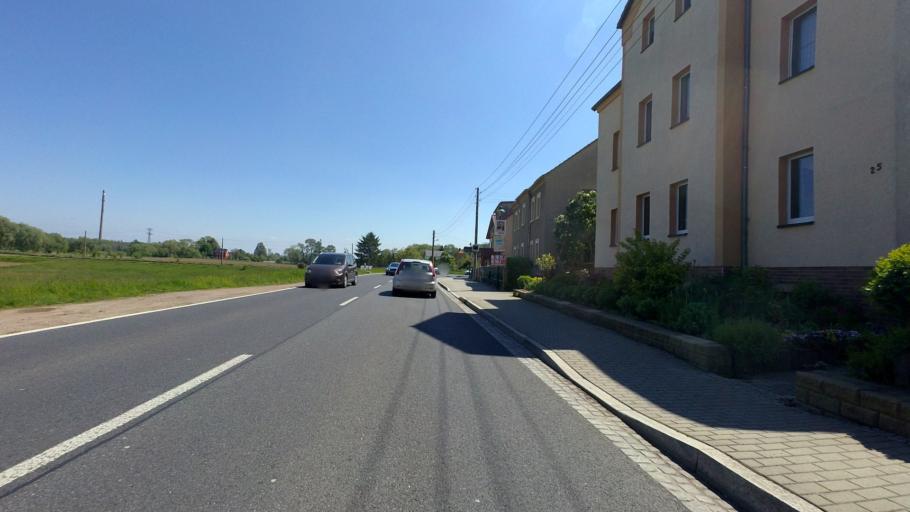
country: DE
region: Saxony
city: Coswig
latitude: 51.1122
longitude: 13.5666
